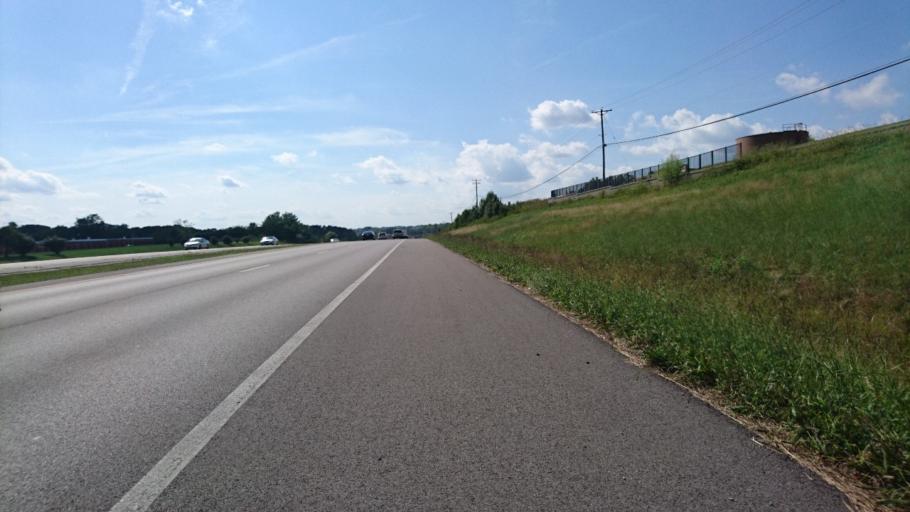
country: US
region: Missouri
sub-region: Saint Louis County
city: Ellisville
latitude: 38.5890
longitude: -90.6020
